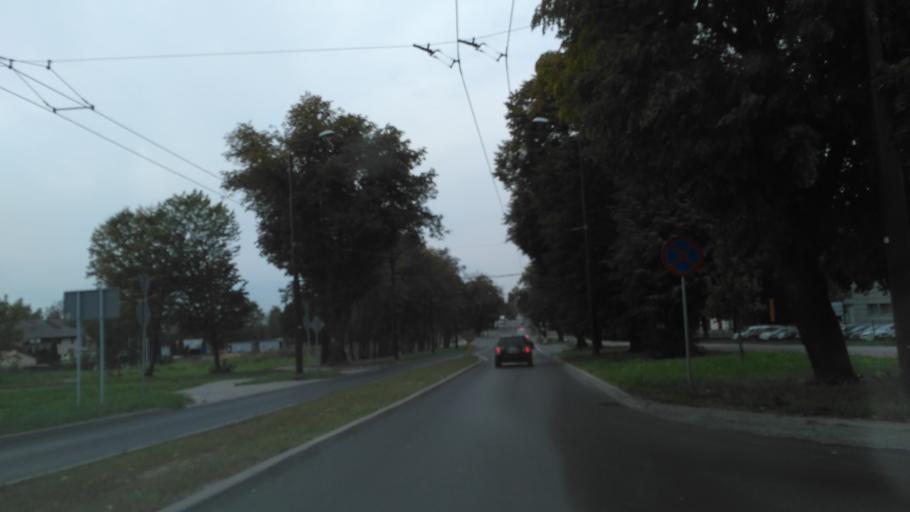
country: PL
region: Lublin Voivodeship
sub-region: Powiat lubelski
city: Jakubowice Murowane
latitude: 51.2238
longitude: 22.6122
